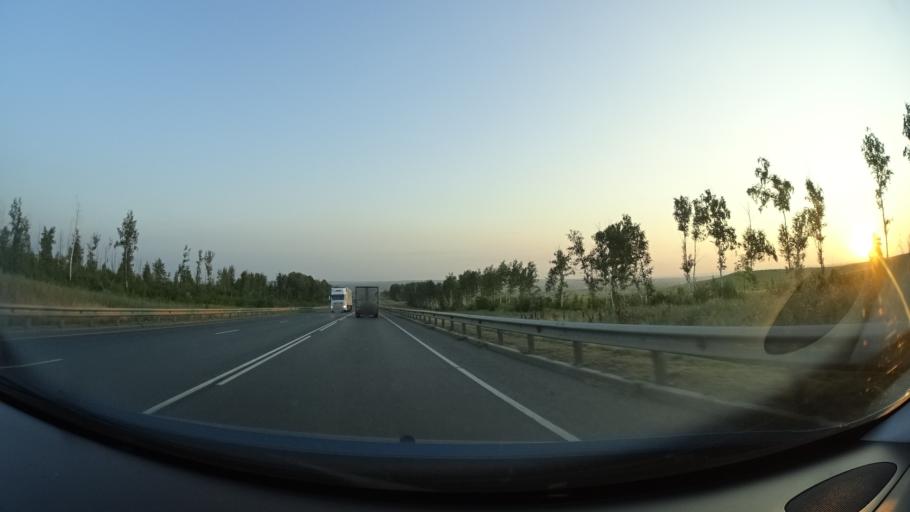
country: RU
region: Samara
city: Sernovodsk
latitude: 53.9088
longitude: 51.2920
